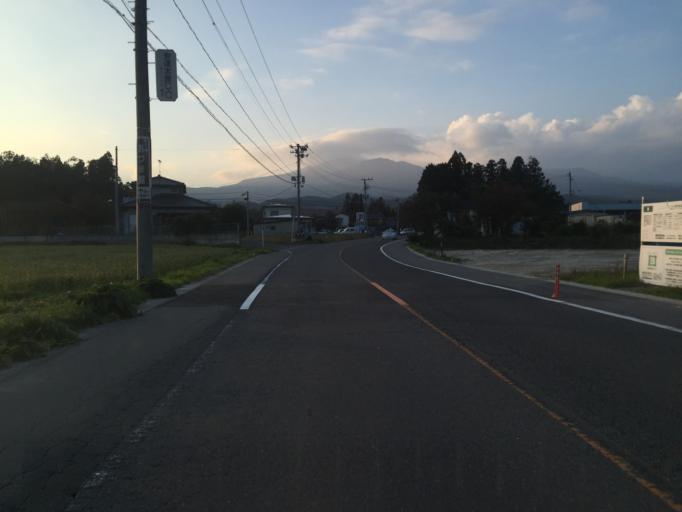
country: JP
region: Fukushima
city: Motomiya
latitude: 37.5557
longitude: 140.3566
